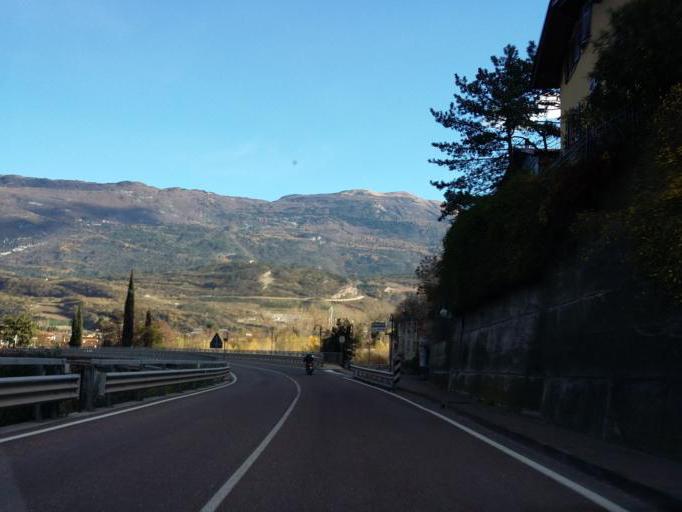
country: IT
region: Trentino-Alto Adige
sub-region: Provincia di Trento
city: Pietramurata
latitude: 46.0463
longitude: 10.9462
